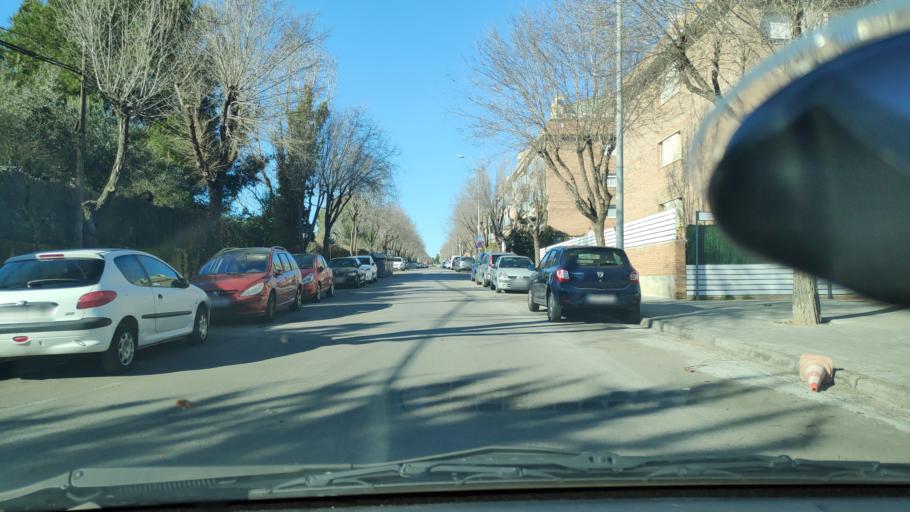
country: ES
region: Catalonia
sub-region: Provincia de Barcelona
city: Sant Quirze del Valles
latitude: 41.5355
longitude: 2.0714
